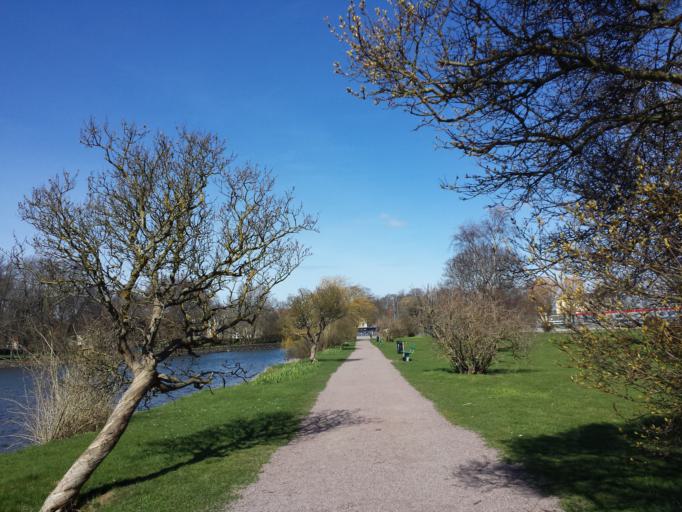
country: SE
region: Kalmar
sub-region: Kalmar Kommun
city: Kalmar
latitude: 56.6601
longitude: 16.3587
